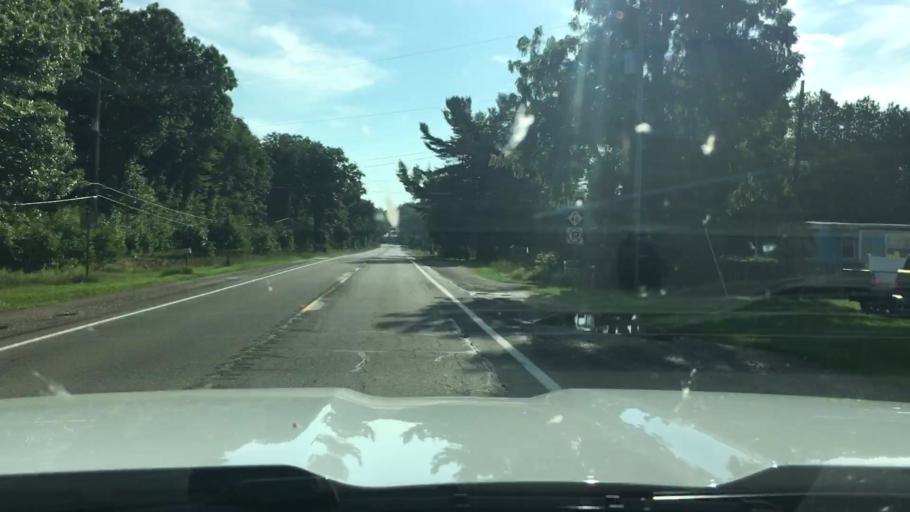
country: US
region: Michigan
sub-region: Kent County
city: Sparta
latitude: 43.2197
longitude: -85.6709
